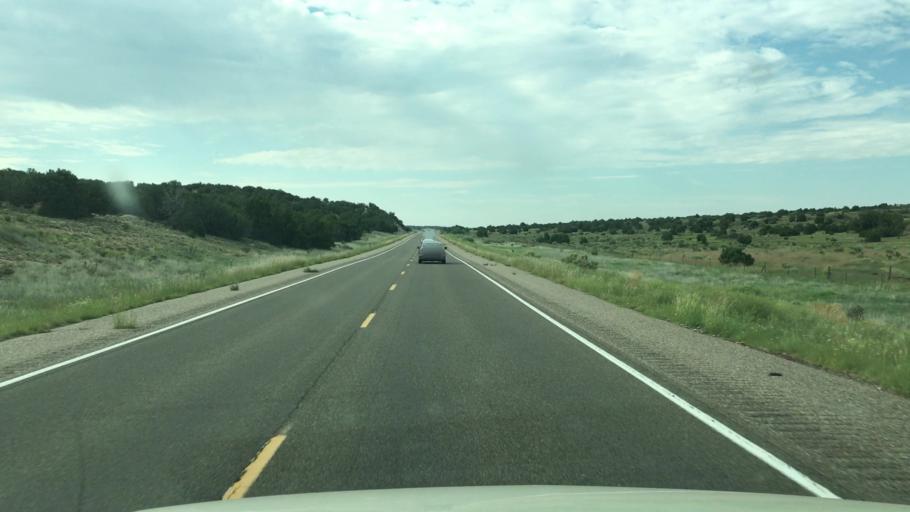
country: US
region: New Mexico
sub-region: Santa Fe County
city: Eldorado at Santa Fe
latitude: 35.3016
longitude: -105.8275
